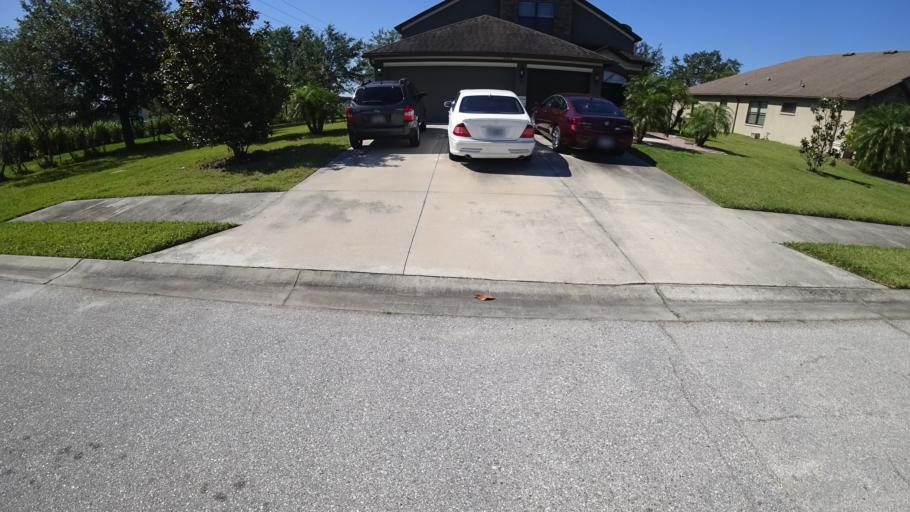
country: US
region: Florida
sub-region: Manatee County
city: Ellenton
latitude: 27.5675
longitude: -82.4338
